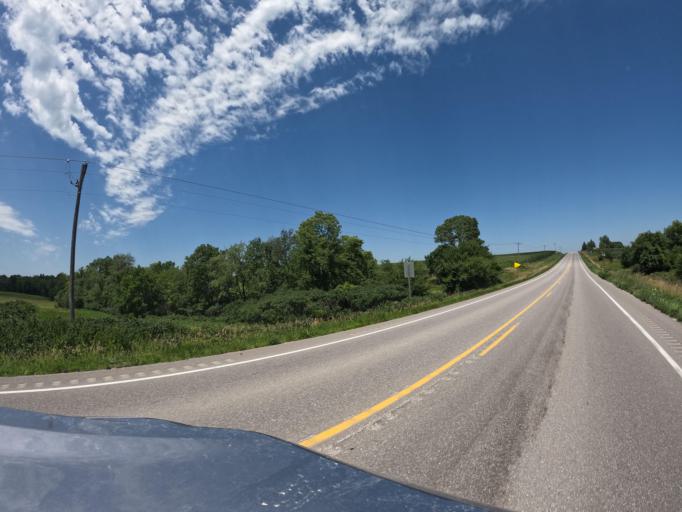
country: US
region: Iowa
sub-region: Keokuk County
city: Sigourney
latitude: 41.4117
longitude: -92.3546
